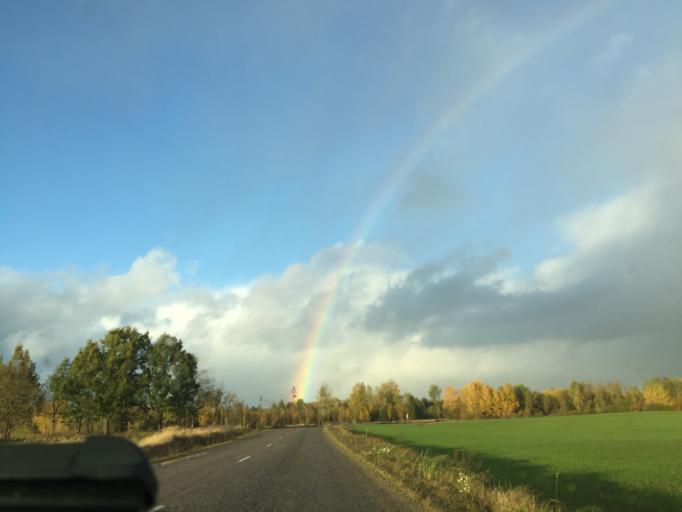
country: LV
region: Broceni
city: Broceni
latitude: 56.8818
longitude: 22.3836
